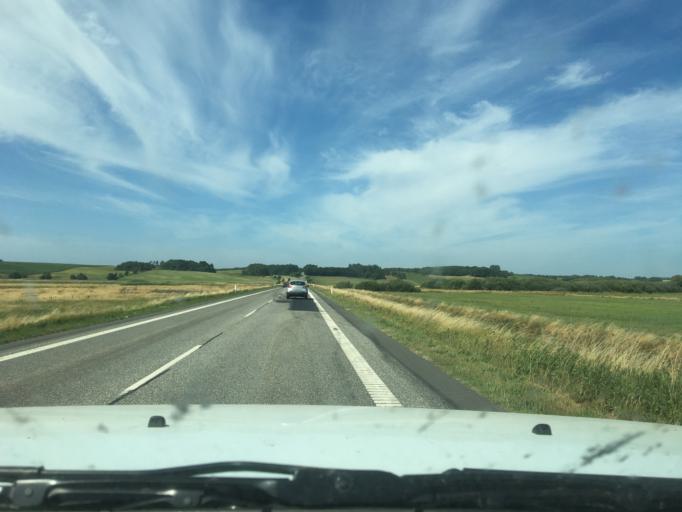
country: DK
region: Central Jutland
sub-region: Viborg Kommune
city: Viborg
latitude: 56.5357
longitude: 9.4034
